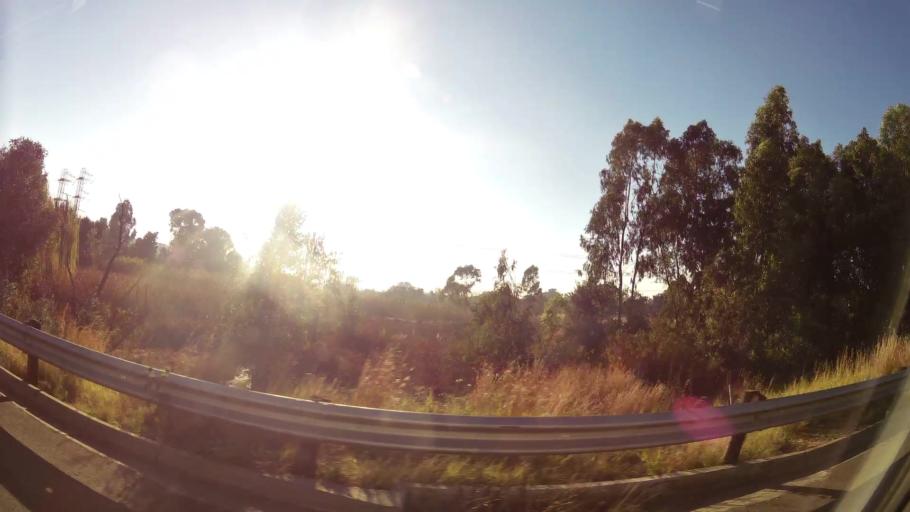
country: ZA
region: Gauteng
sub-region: City of Johannesburg Metropolitan Municipality
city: Johannesburg
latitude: -26.2667
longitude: 28.0973
